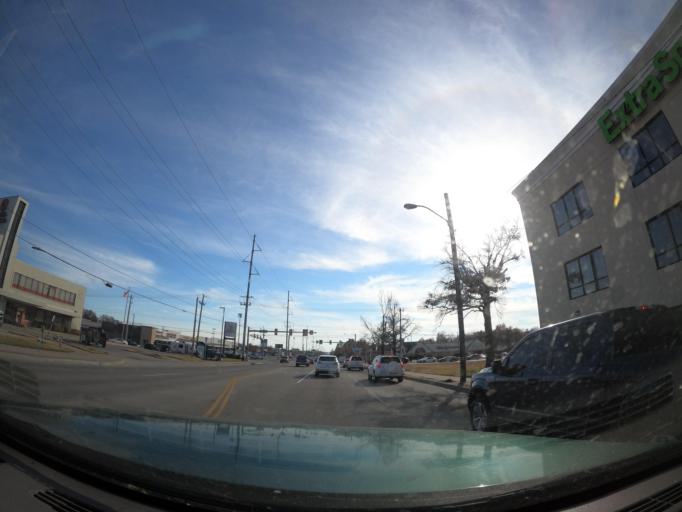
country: US
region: Oklahoma
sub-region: Tulsa County
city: Tulsa
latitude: 36.1195
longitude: -95.9403
